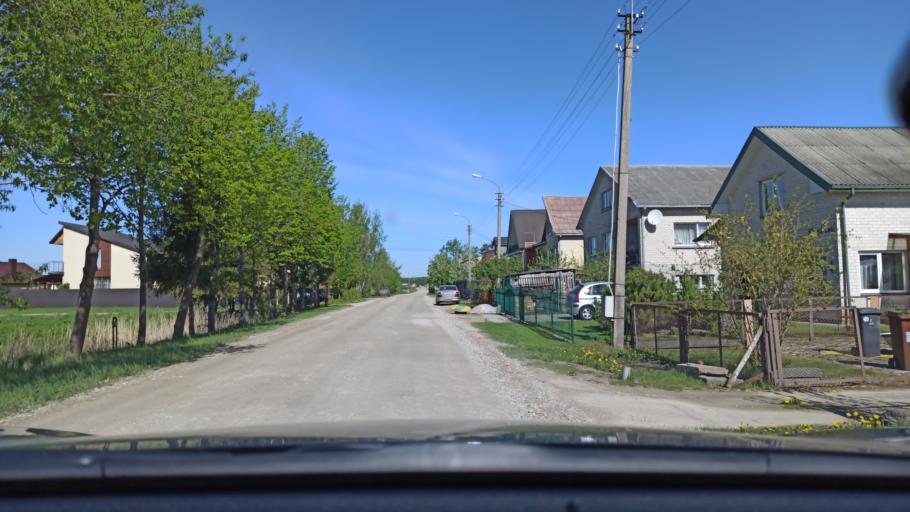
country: LT
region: Siauliu apskritis
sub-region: Siauliai
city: Siauliai
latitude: 55.9587
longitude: 23.2928
